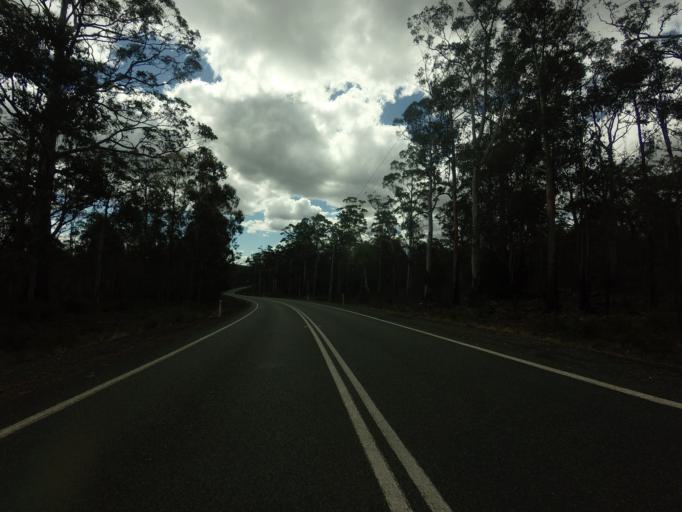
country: AU
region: Tasmania
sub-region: Northern Midlands
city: Evandale
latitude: -41.9929
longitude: 147.7133
